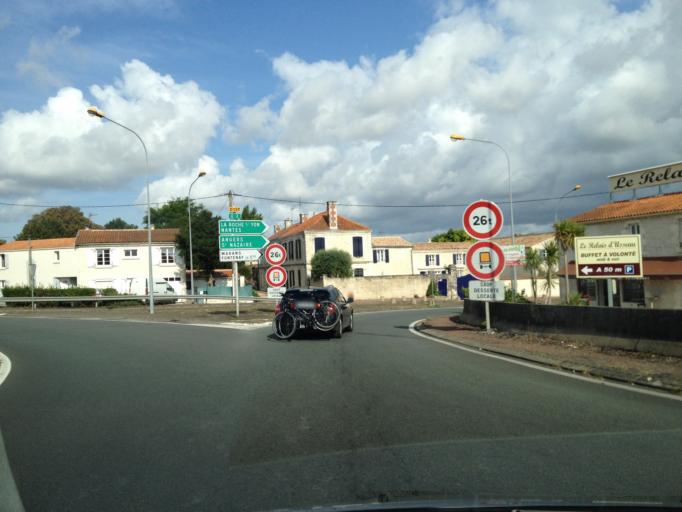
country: FR
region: Poitou-Charentes
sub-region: Departement de la Charente-Maritime
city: Sainte-Soulle
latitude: 46.2028
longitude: -1.0275
